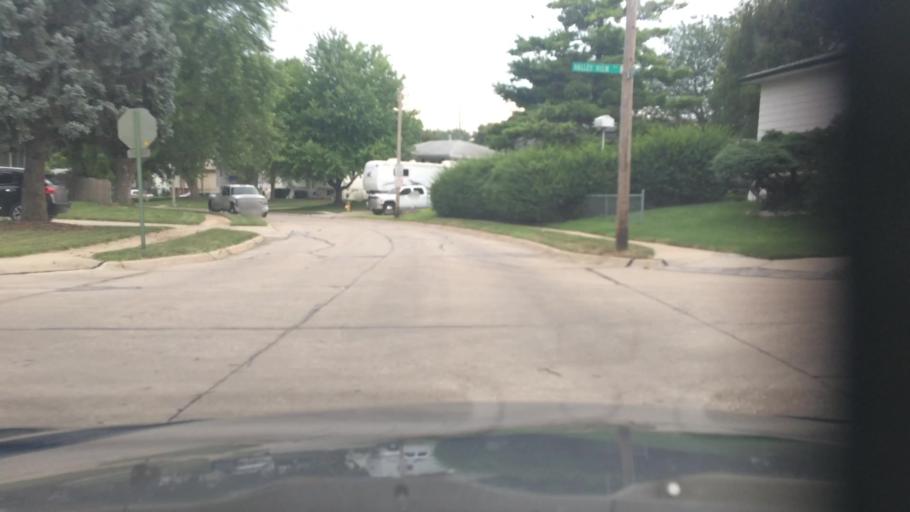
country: US
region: Nebraska
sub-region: Douglas County
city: Ralston
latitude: 41.1871
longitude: -96.0516
